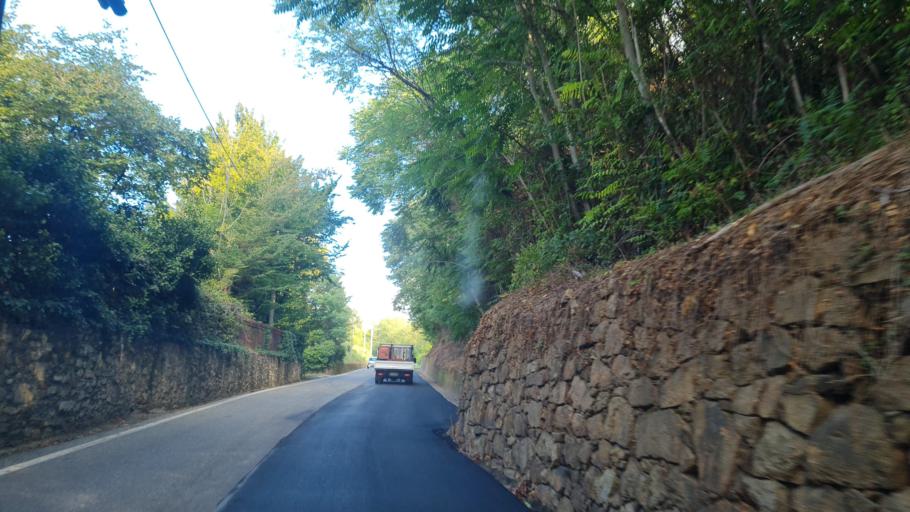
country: IT
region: Piedmont
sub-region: Provincia di Biella
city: Quaregna
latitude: 45.5862
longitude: 8.1623
